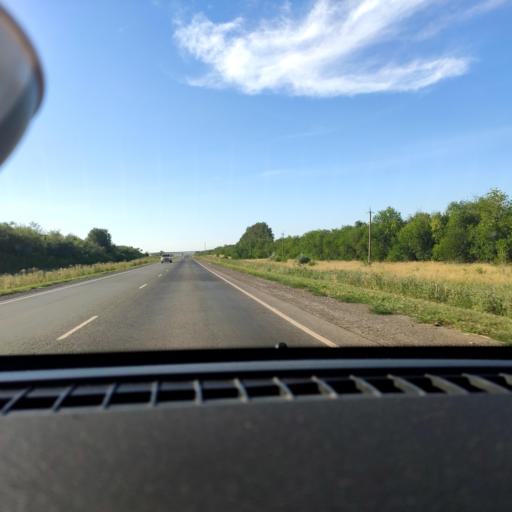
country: RU
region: Samara
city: Krasnoarmeyskoye
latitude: 52.8694
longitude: 49.9861
